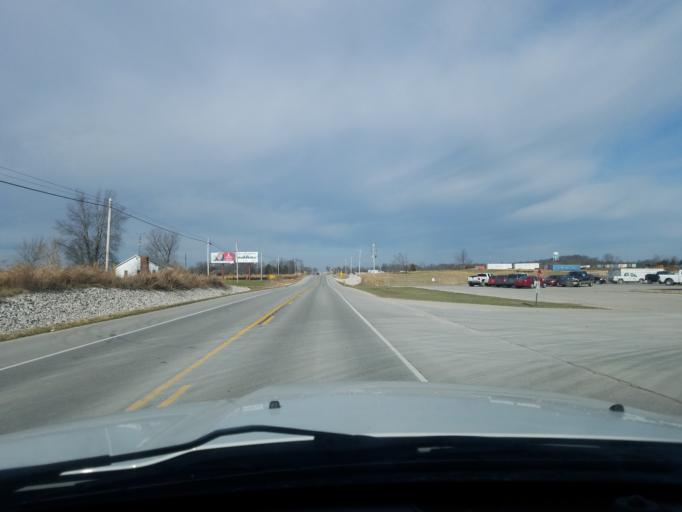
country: US
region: Indiana
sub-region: Orange County
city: Orleans
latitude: 38.6222
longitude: -86.4584
